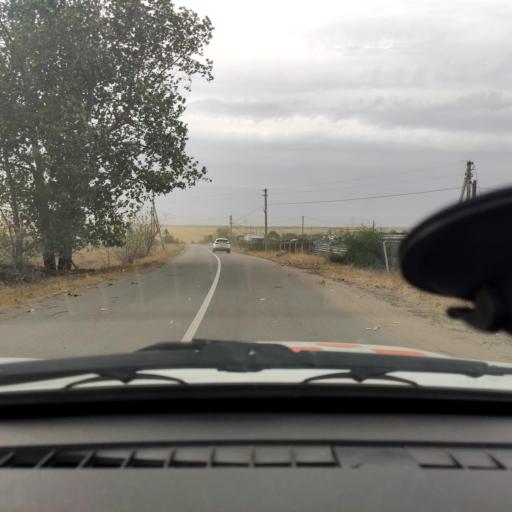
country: RU
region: Lipetsk
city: Khlevnoye
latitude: 52.0054
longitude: 39.1235
